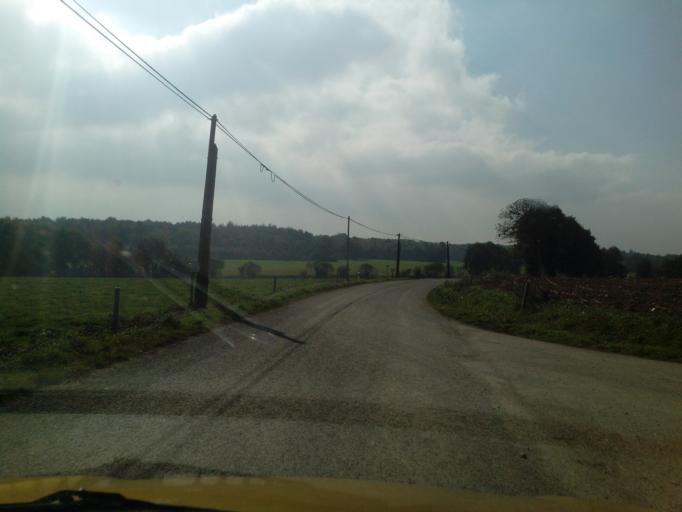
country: FR
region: Brittany
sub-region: Departement du Morbihan
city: Guilliers
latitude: 48.1025
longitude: -2.4008
